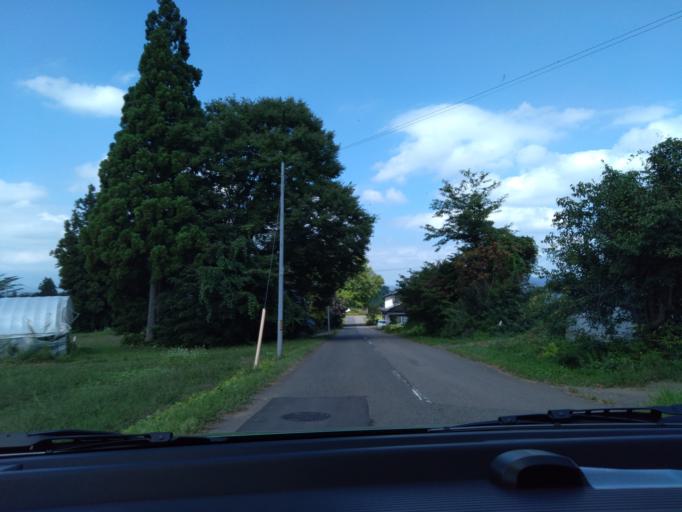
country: JP
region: Iwate
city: Shizukuishi
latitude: 39.6818
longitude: 140.9592
